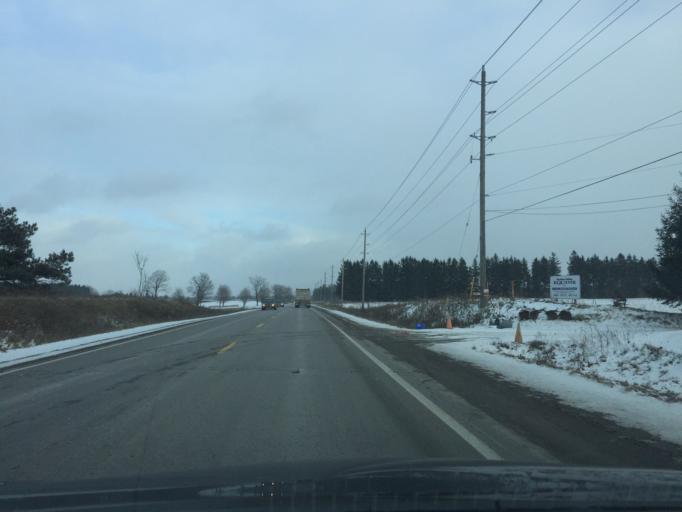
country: CA
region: Ontario
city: Uxbridge
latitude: 44.0371
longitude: -79.1834
